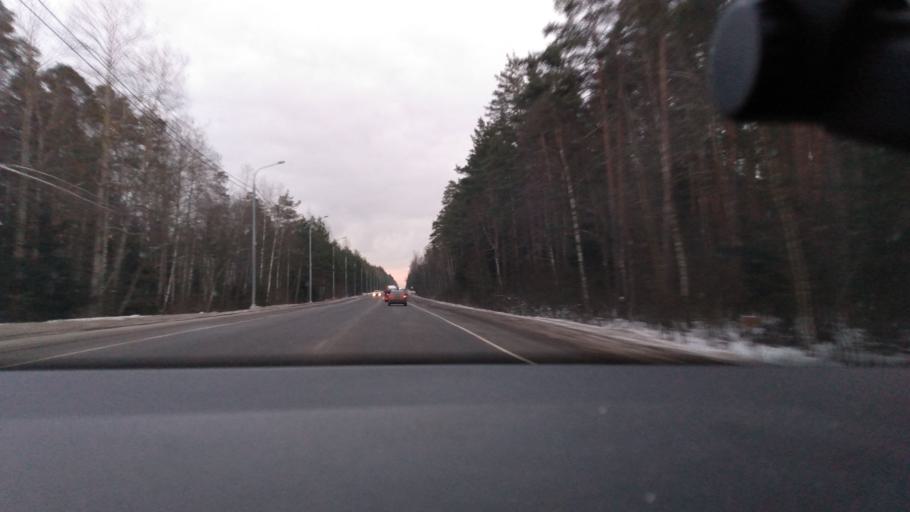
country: RU
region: Moskovskaya
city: Il'inskiy Pogost
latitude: 55.4735
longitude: 38.9559
